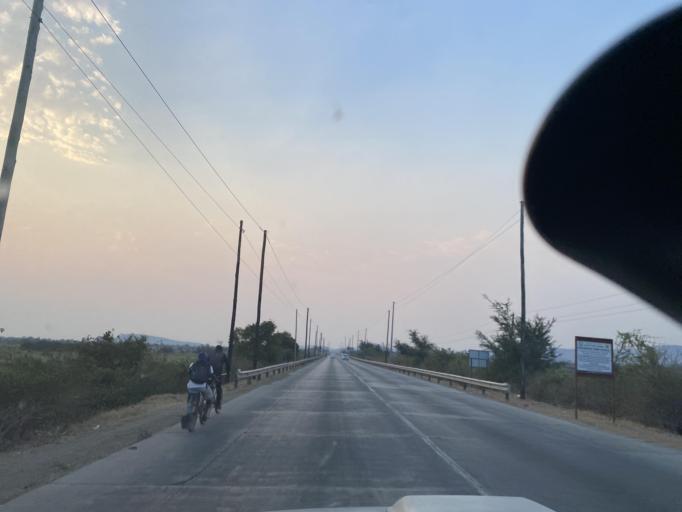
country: ZM
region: Lusaka
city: Kafue
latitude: -15.8412
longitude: 28.2390
